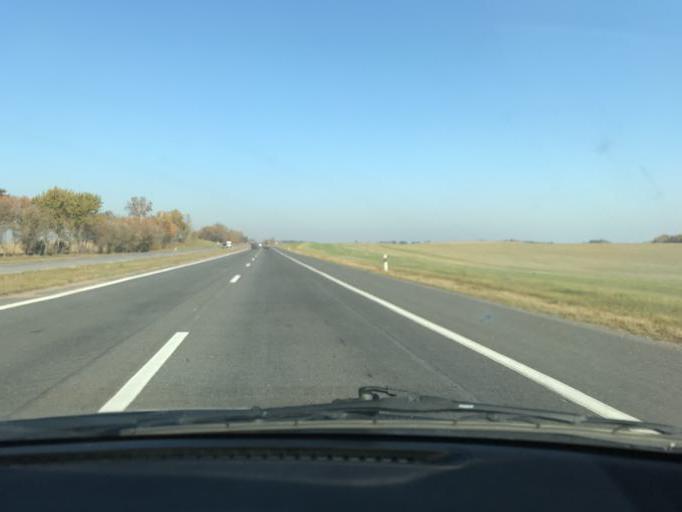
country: BY
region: Minsk
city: Samakhvalavichy
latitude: 53.6814
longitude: 27.5057
